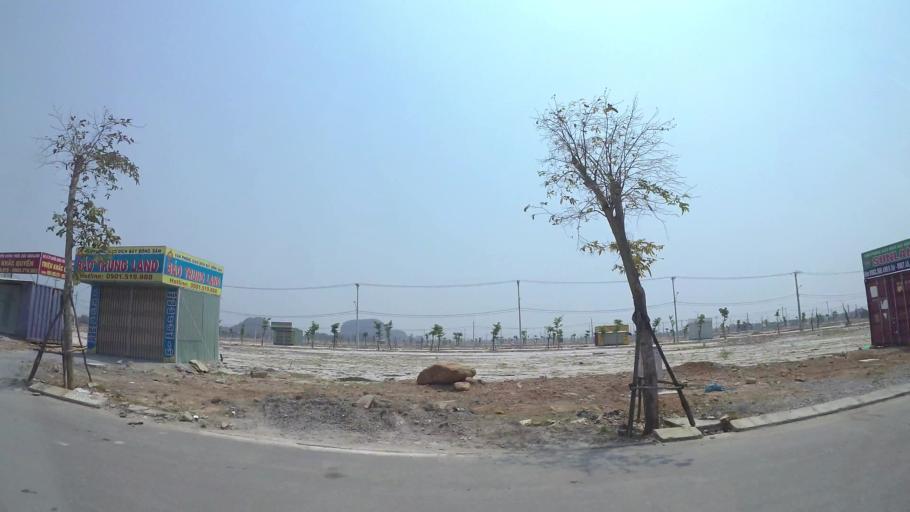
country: VN
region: Da Nang
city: Ngu Hanh Son
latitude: 16.0116
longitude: 108.2453
